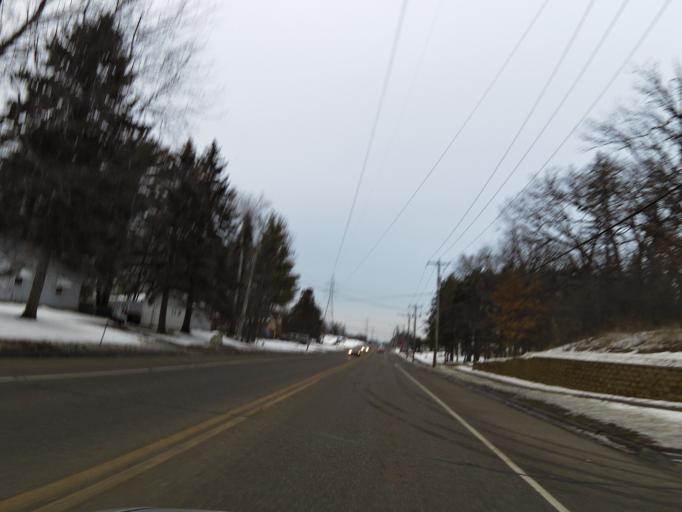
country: US
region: Minnesota
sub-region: Washington County
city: Oakdale
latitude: 44.9841
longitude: -92.9646
